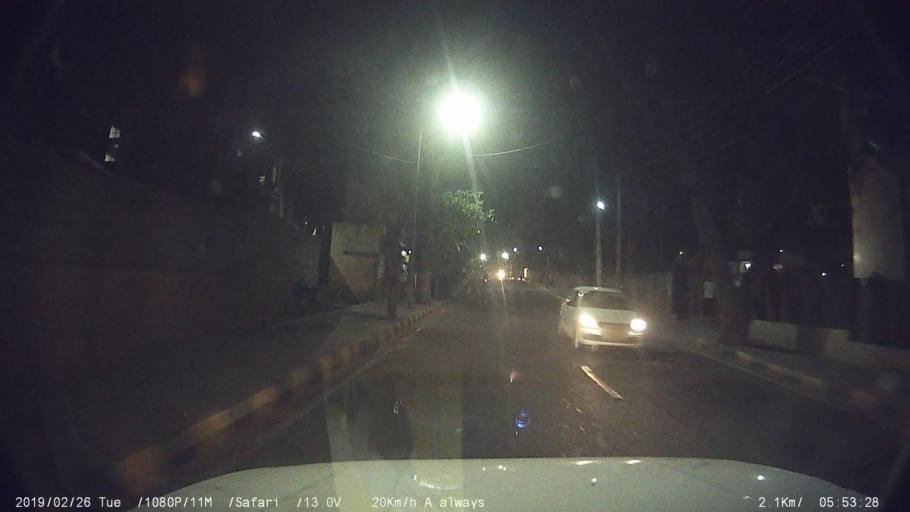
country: IN
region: Karnataka
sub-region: Bangalore Urban
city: Bangalore
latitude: 12.8494
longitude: 77.6630
